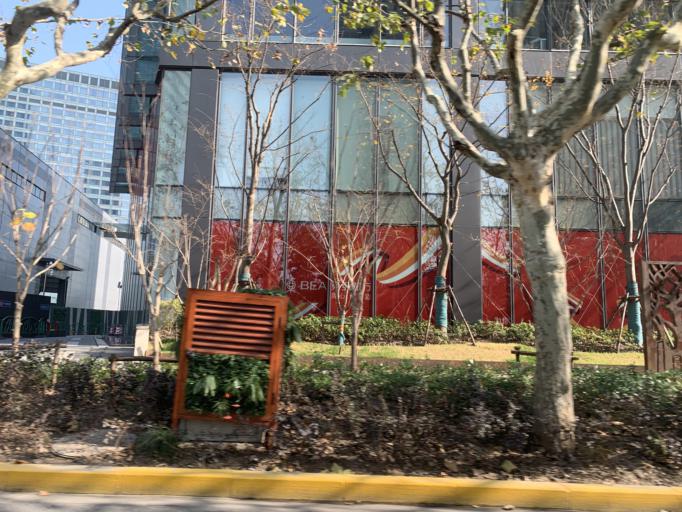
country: CN
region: Shanghai Shi
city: Hongkou
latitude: 31.2359
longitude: 121.4974
